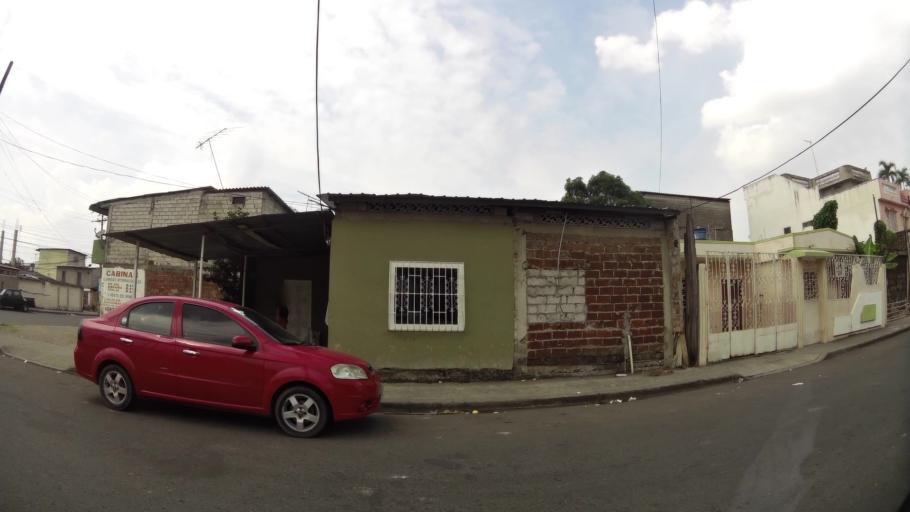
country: EC
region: Guayas
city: Guayaquil
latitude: -2.2352
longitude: -79.9055
